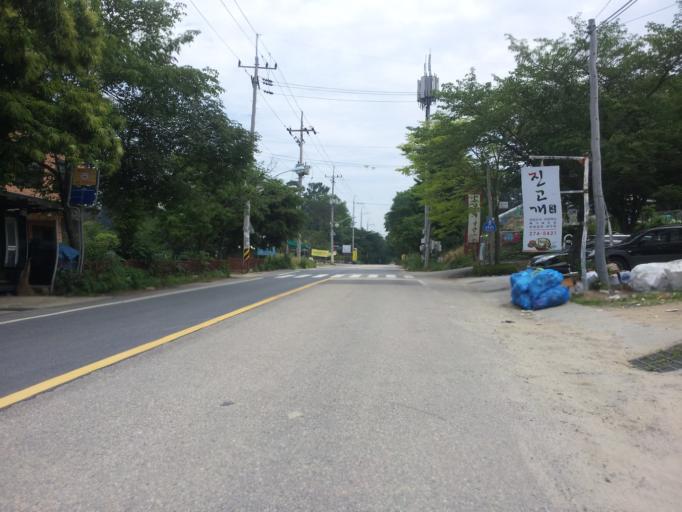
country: KR
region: Chungcheongbuk-do
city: Okcheon
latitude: 36.3654
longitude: 127.5031
